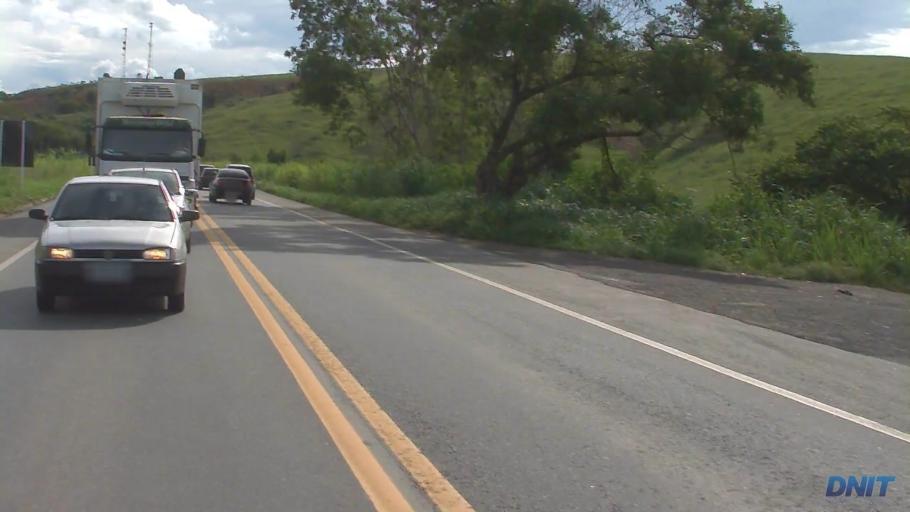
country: BR
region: Minas Gerais
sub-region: Belo Oriente
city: Belo Oriente
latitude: -19.2173
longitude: -42.3069
